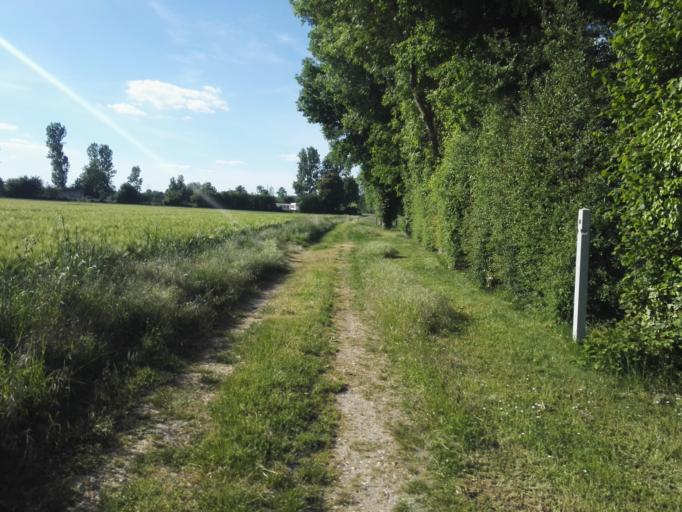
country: FR
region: Haute-Normandie
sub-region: Departement de l'Eure
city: Pacy-sur-Eure
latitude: 48.9889
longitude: 1.3981
